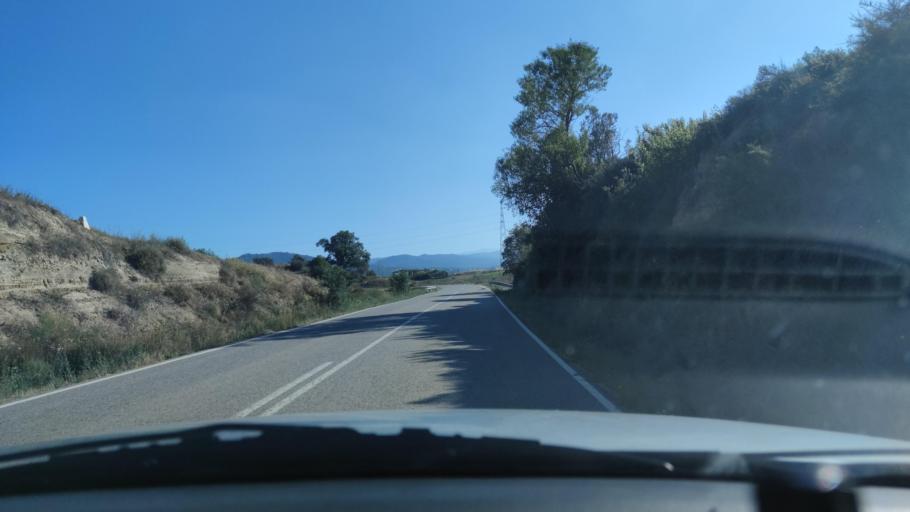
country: ES
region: Catalonia
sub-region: Provincia de Lleida
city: Ponts
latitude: 41.8988
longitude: 1.2383
